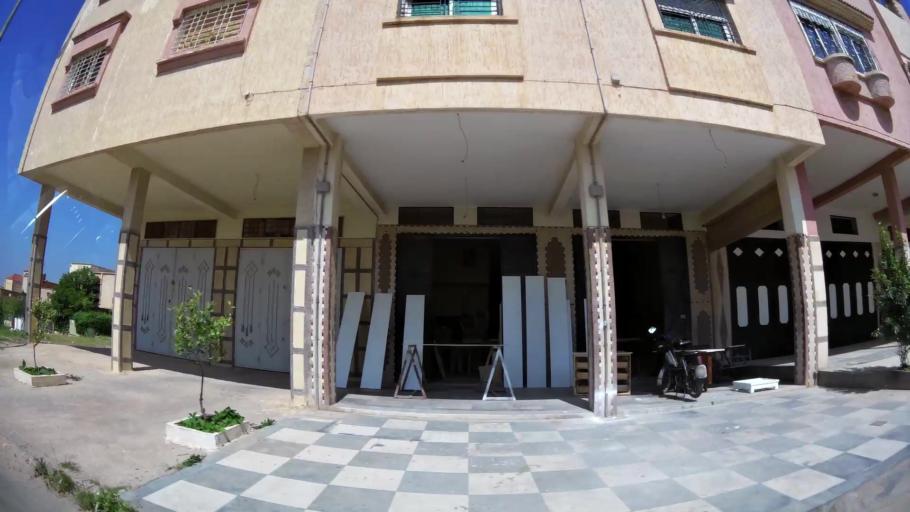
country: MA
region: Oriental
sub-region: Oujda-Angad
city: Oujda
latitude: 34.6895
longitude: -1.8737
